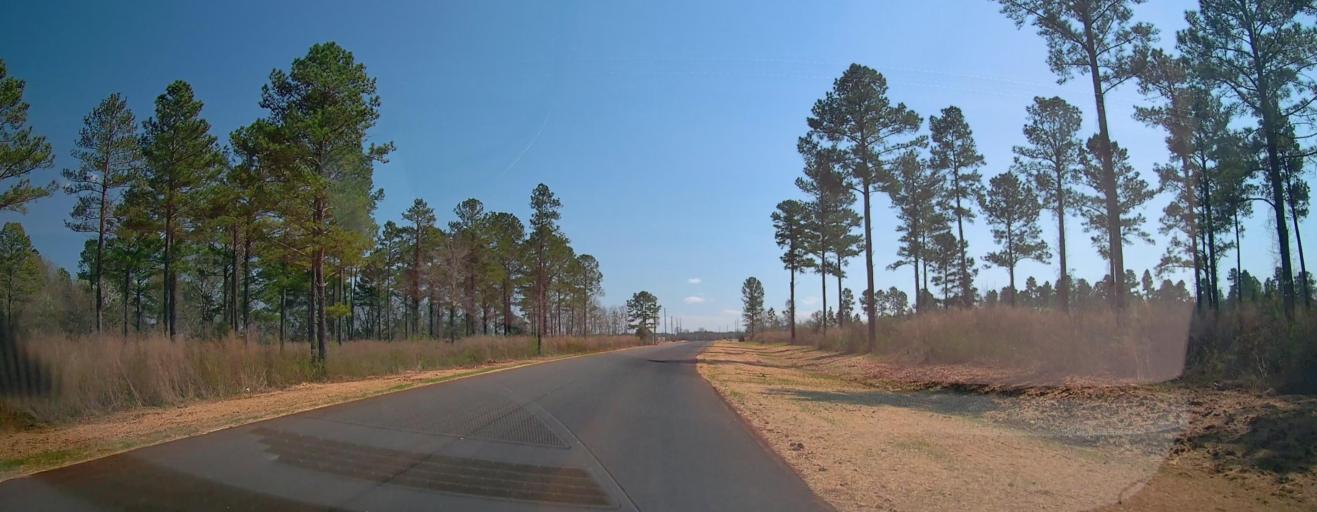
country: US
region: Georgia
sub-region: Houston County
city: Centerville
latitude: 32.6011
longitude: -83.7306
